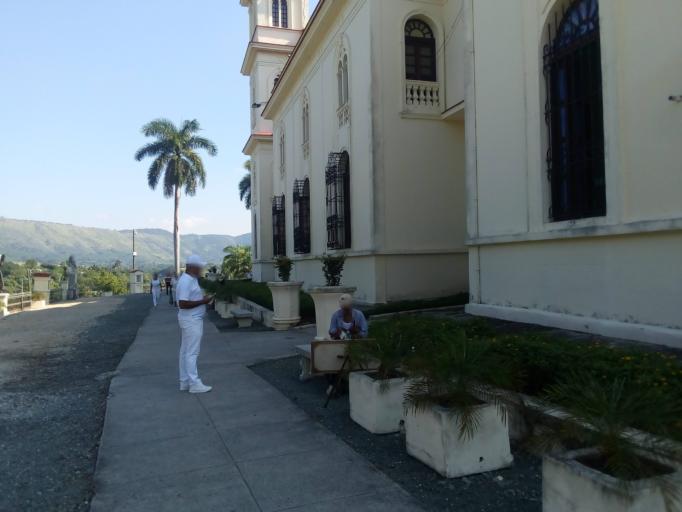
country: CU
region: Santiago de Cuba
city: El Cobre
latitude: 20.0507
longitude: -75.9494
